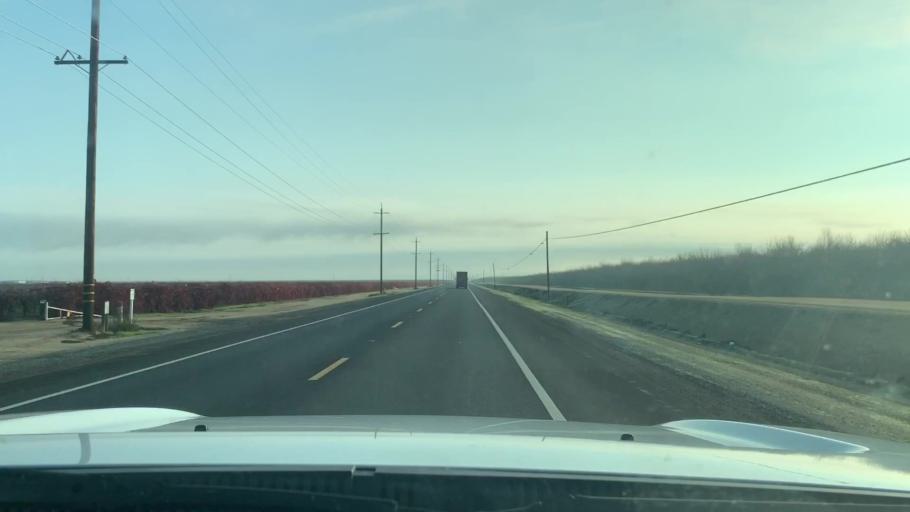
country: US
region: California
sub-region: Kern County
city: Wasco
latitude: 35.6017
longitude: -119.2728
